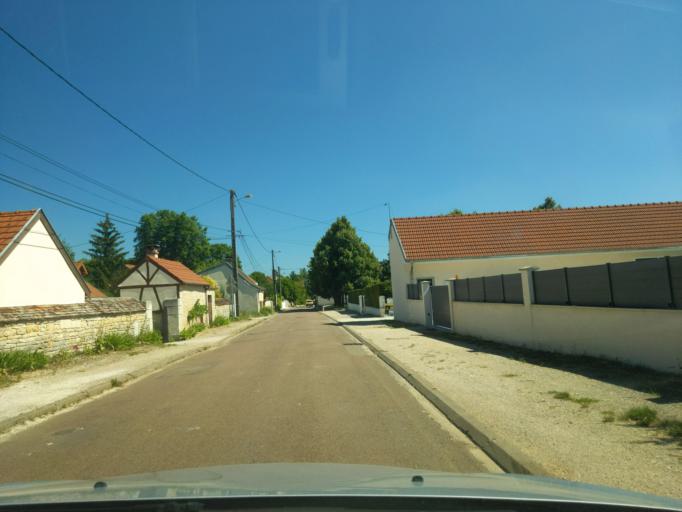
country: FR
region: Bourgogne
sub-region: Departement de la Cote-d'Or
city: Ruffey-les-Echirey
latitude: 47.3992
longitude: 5.0855
